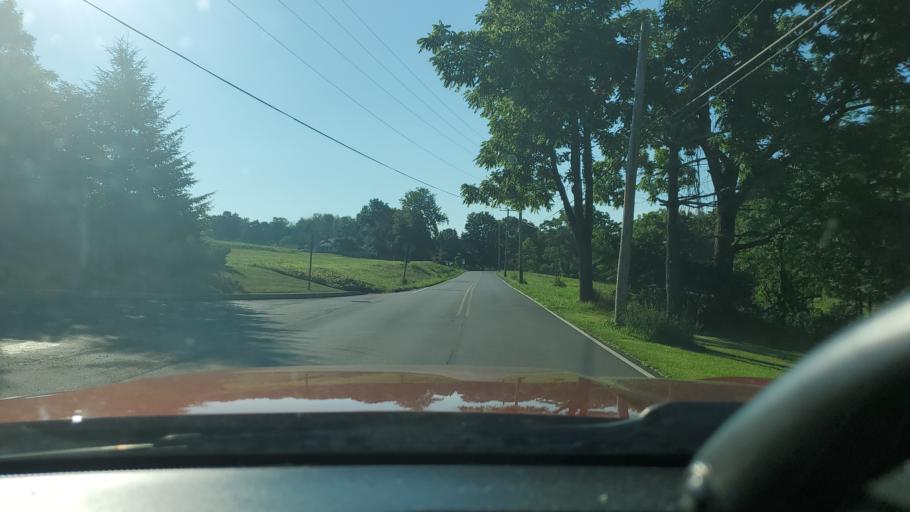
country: US
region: Pennsylvania
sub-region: Montgomery County
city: Harleysville
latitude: 40.2972
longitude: -75.3839
